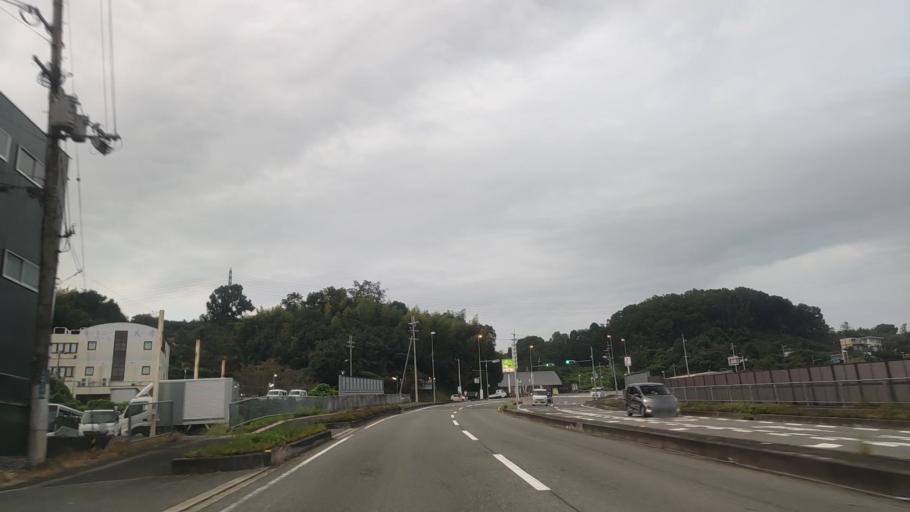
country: JP
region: Wakayama
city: Hashimoto
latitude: 34.3161
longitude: 135.6019
